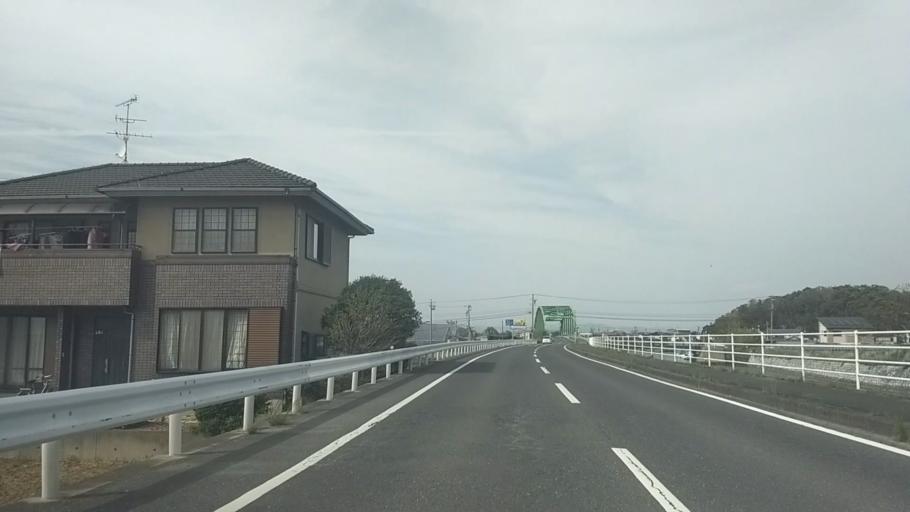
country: JP
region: Shizuoka
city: Kosai-shi
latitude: 34.7075
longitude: 137.6177
